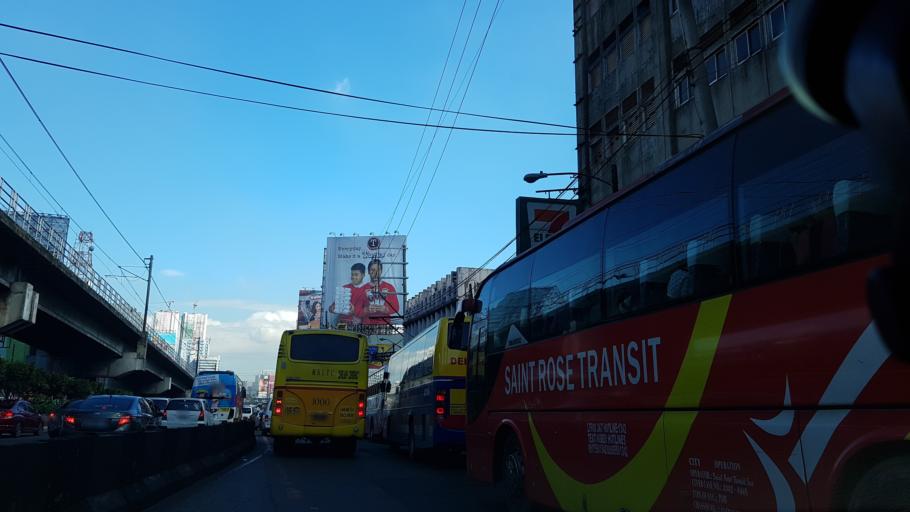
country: PH
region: Metro Manila
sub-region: Quezon City
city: Quezon City
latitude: 14.6238
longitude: 121.0492
